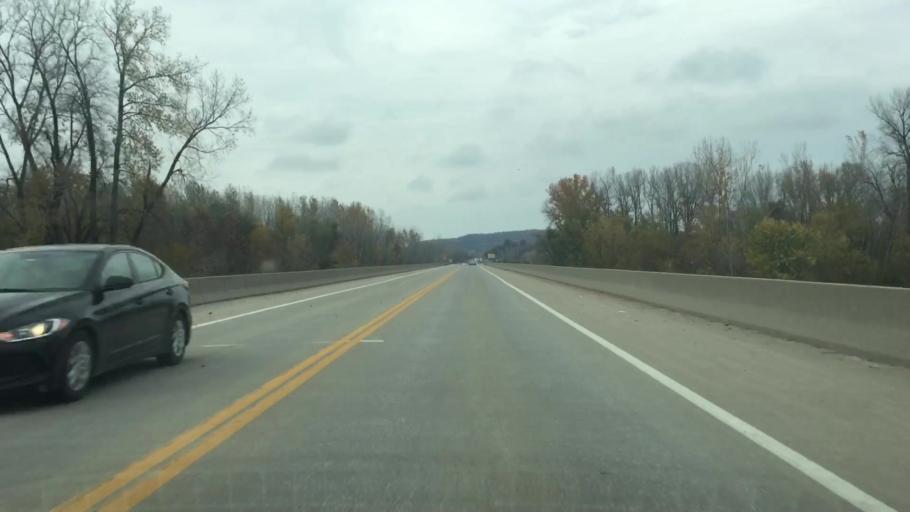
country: US
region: Missouri
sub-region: Gasconade County
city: Hermann
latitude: 38.7177
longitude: -91.4420
